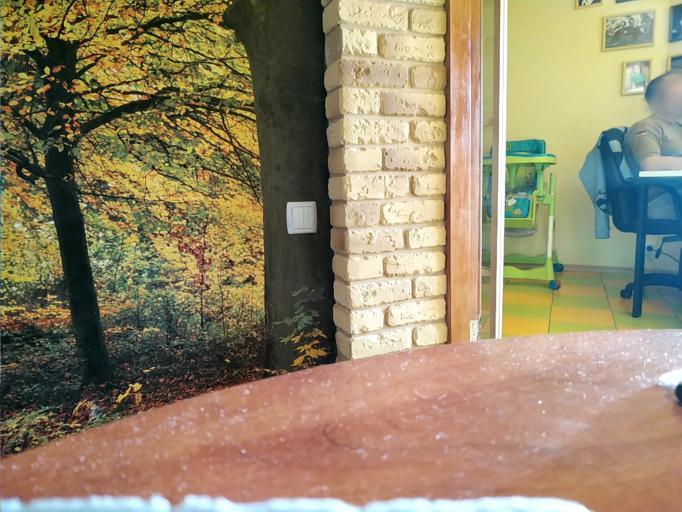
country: RU
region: Tverskaya
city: Rameshki
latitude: 57.3149
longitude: 35.9066
